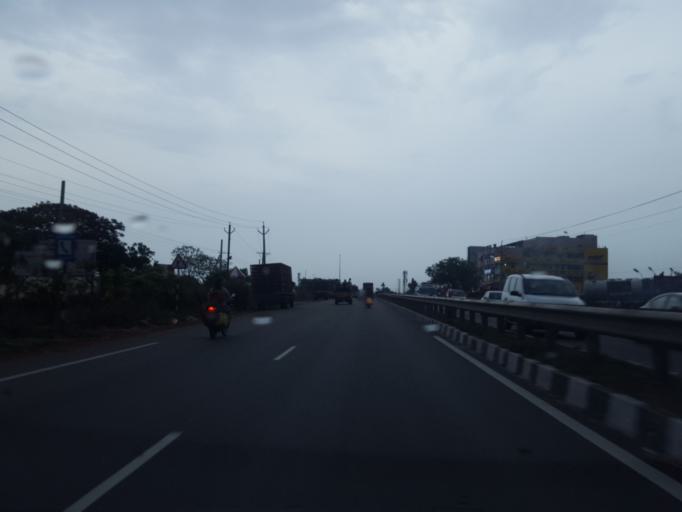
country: IN
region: Telangana
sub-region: Mahbubnagar
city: Farrukhnagar
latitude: 17.1535
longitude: 78.2919
